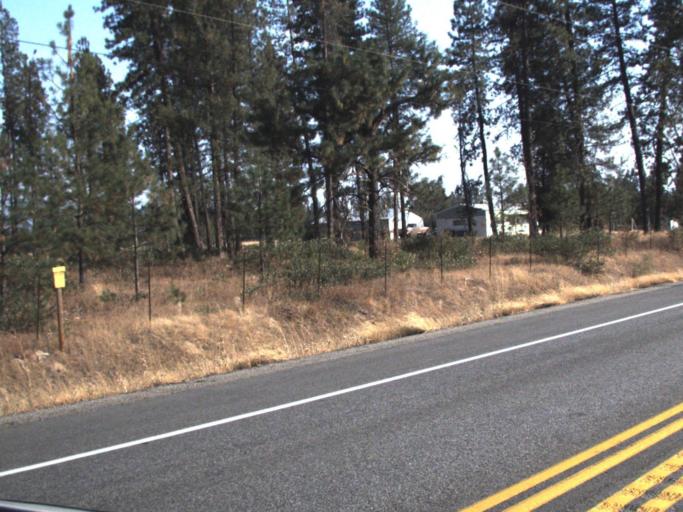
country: US
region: Washington
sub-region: Spokane County
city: Deer Park
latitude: 48.0305
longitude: -117.3498
